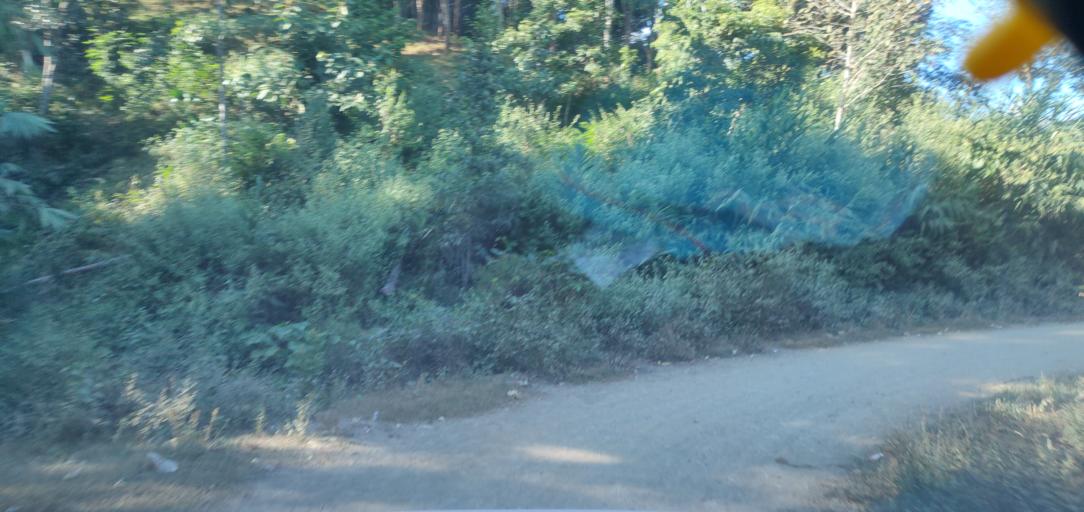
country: LA
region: Phongsali
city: Phongsali
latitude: 21.4893
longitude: 102.0915
